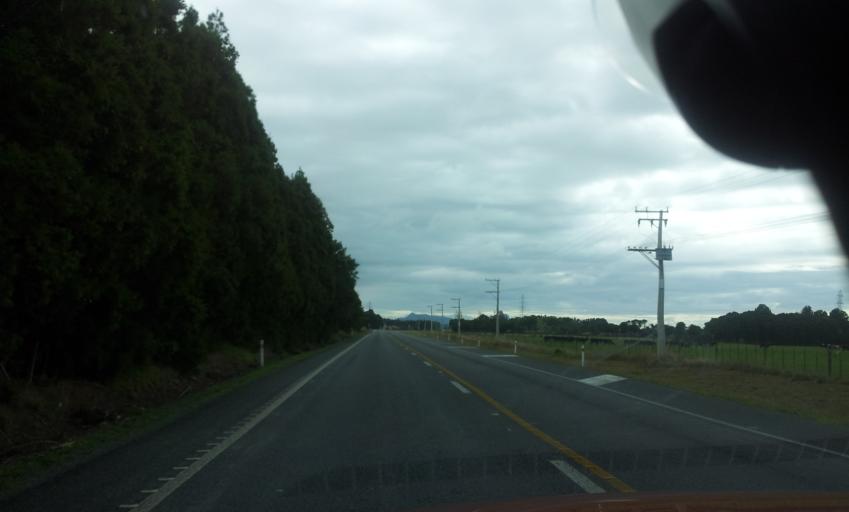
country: NZ
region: Northland
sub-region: Whangarei
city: Ruakaka
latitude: -35.9967
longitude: 174.4186
